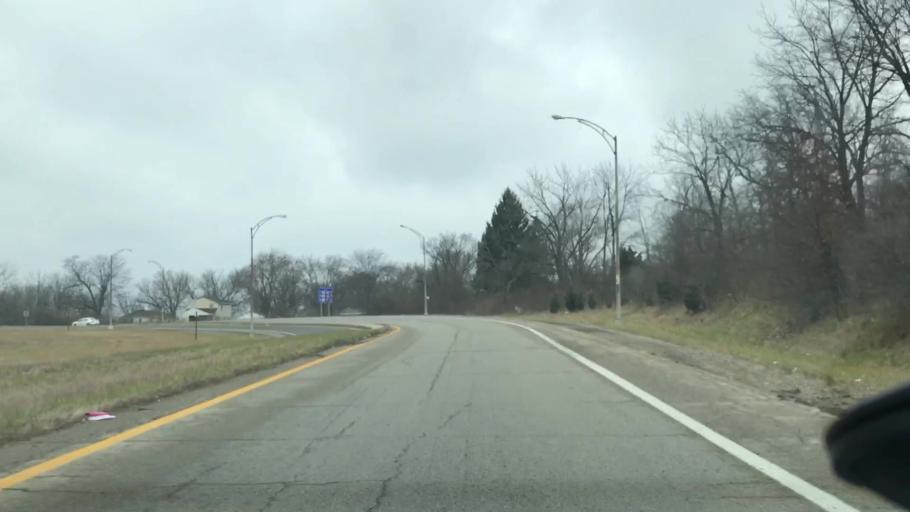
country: US
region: Ohio
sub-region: Franklin County
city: Lincoln Village
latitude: 39.9757
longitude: -83.0982
